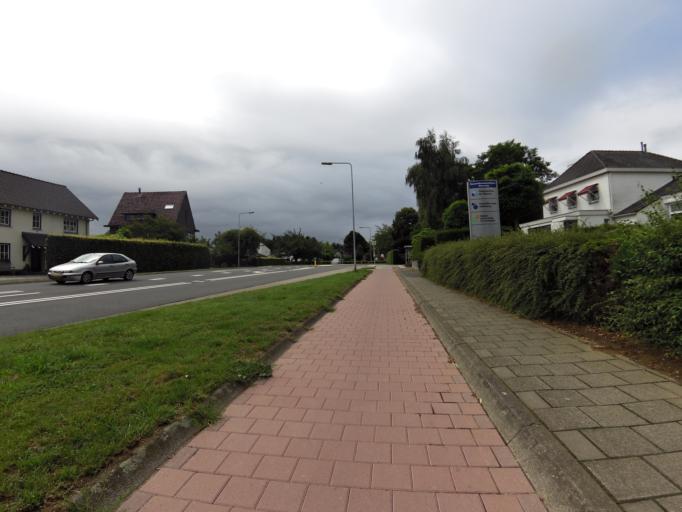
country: NL
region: Limburg
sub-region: Gemeente Voerendaal
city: Klimmen
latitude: 50.8909
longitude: 5.8550
